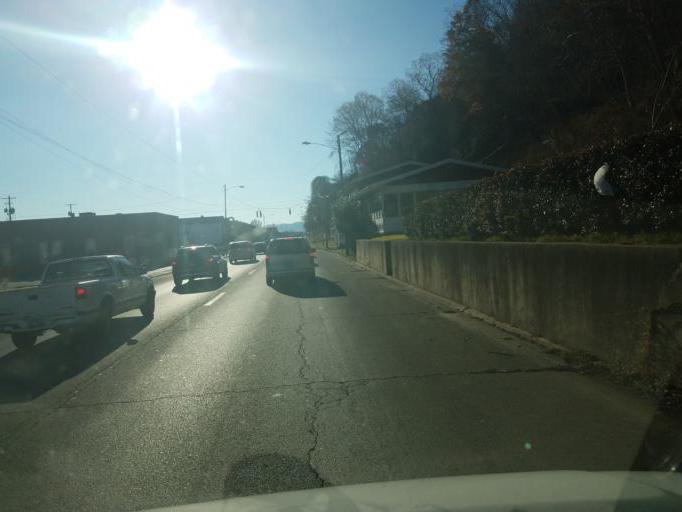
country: US
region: Ohio
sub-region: Scioto County
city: New Boston
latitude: 38.7523
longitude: -82.9374
